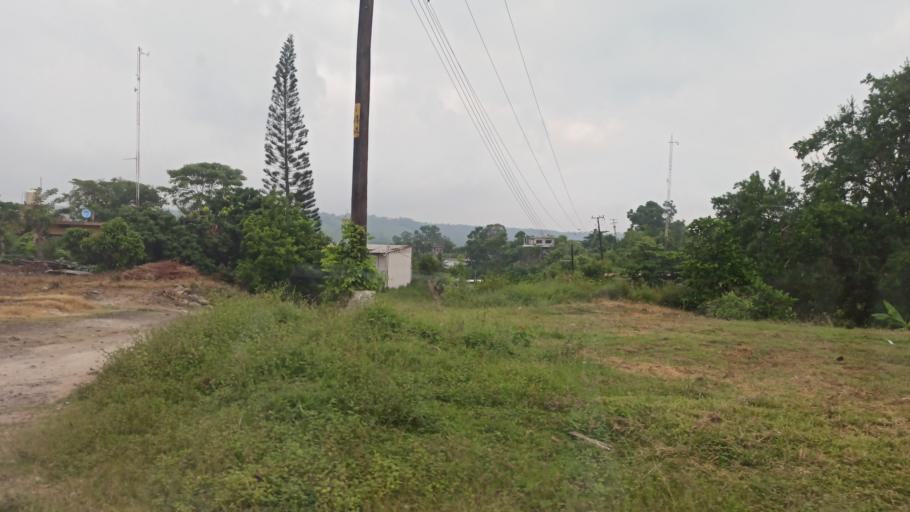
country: MX
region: Puebla
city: San Jose Acateno
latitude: 20.2289
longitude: -97.1235
